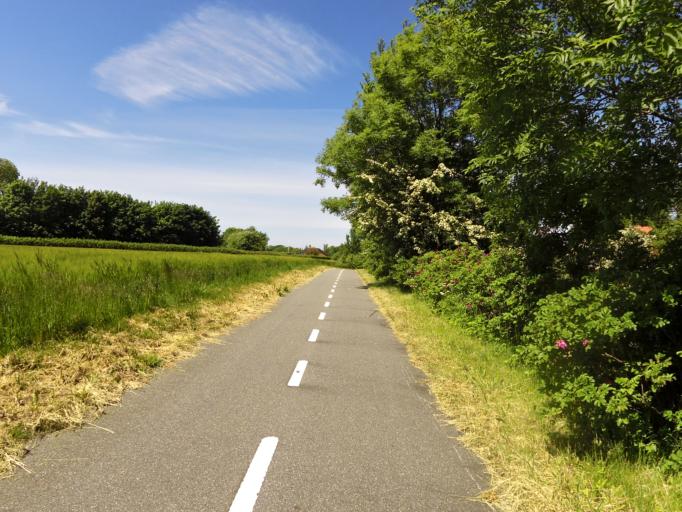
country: DK
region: South Denmark
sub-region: Haderslev Kommune
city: Gram
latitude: 55.2743
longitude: 9.0717
